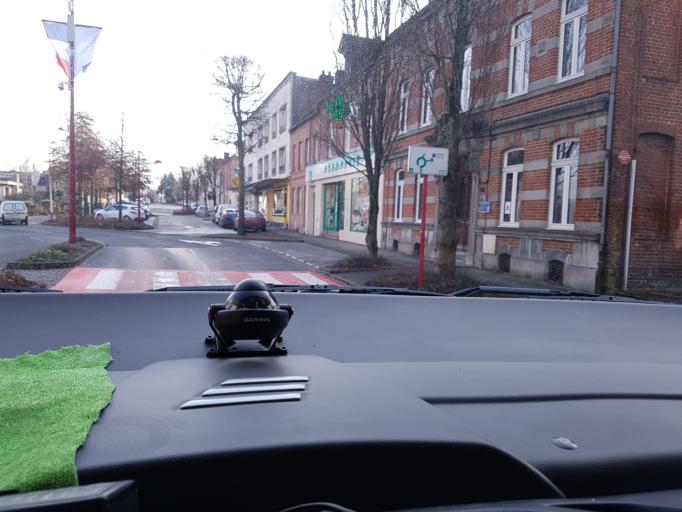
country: FR
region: Picardie
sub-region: Departement de l'Aisne
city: Hirson
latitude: 49.9176
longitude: 4.0856
